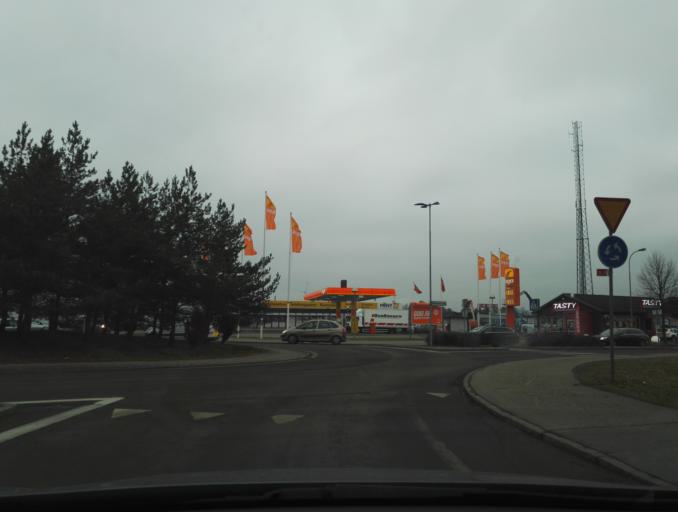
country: SE
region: Kronoberg
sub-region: Vaxjo Kommun
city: Vaexjoe
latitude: 56.8876
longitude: 14.7793
